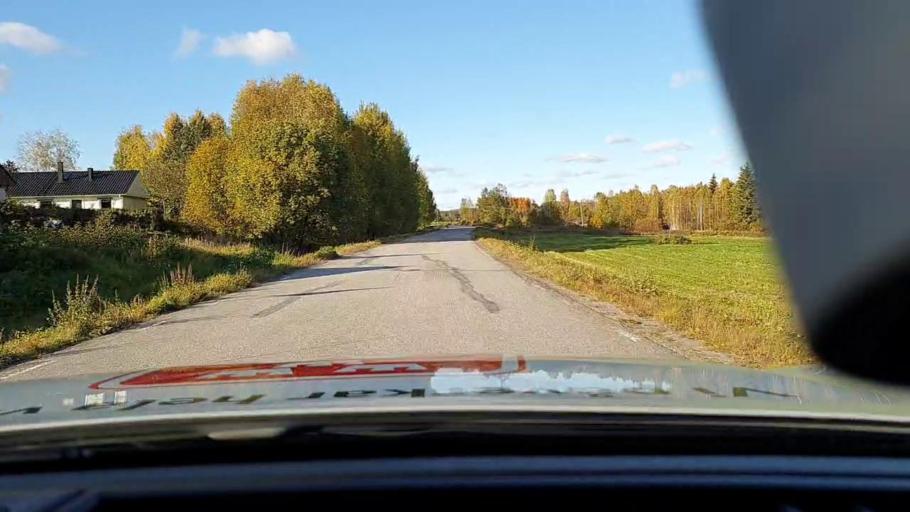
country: SE
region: Norrbotten
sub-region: Pitea Kommun
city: Norrfjarden
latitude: 65.5179
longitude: 21.4949
